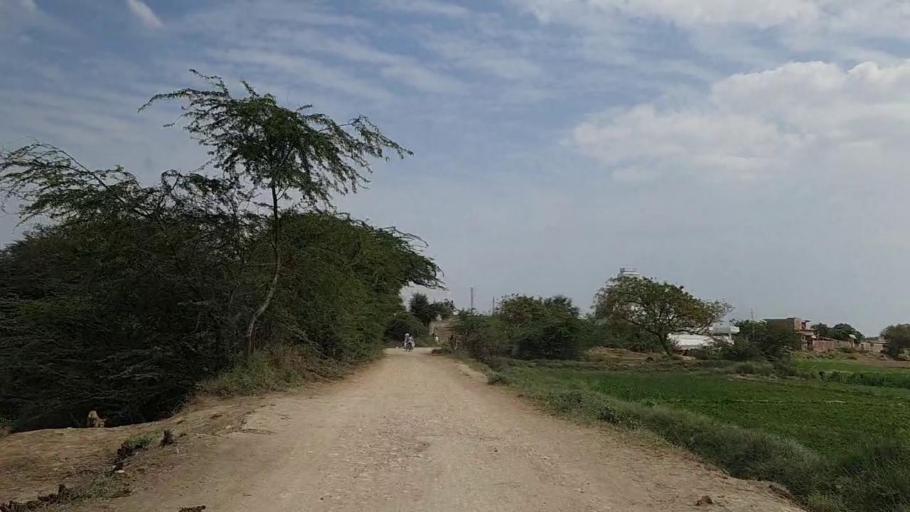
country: PK
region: Sindh
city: Daro Mehar
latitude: 24.8437
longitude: 68.1935
